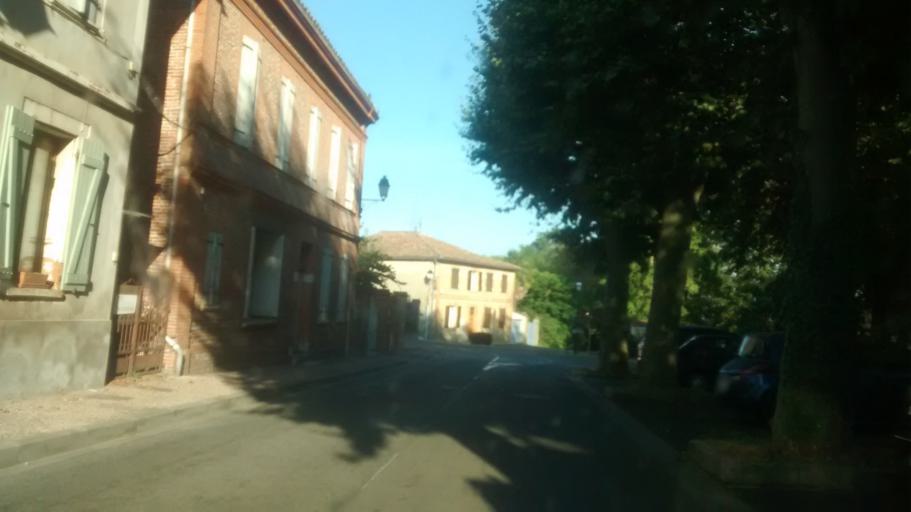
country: FR
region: Midi-Pyrenees
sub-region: Departement de la Haute-Garonne
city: Lherm
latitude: 43.4302
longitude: 1.2233
